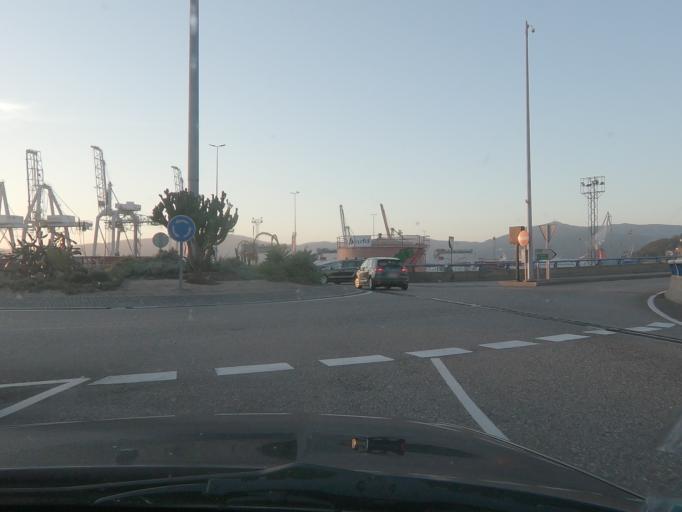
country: ES
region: Galicia
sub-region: Provincia de Pontevedra
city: Vigo
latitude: 42.2421
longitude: -8.7075
